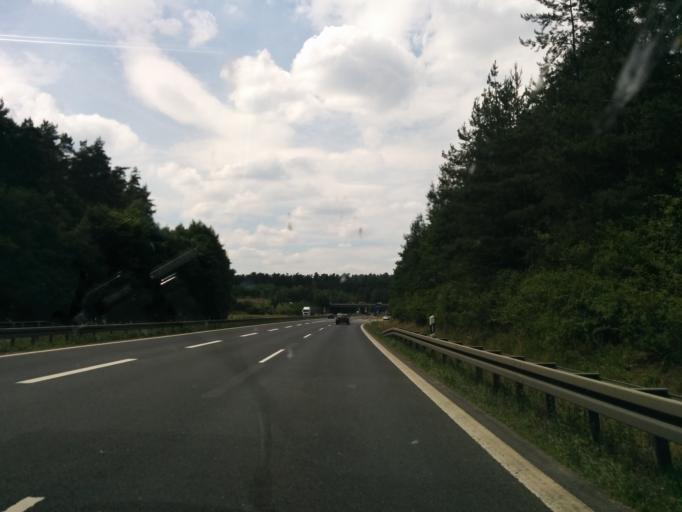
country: DE
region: Bavaria
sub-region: Regierungsbezirk Mittelfranken
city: Rednitzhembach
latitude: 49.3315
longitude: 11.0650
